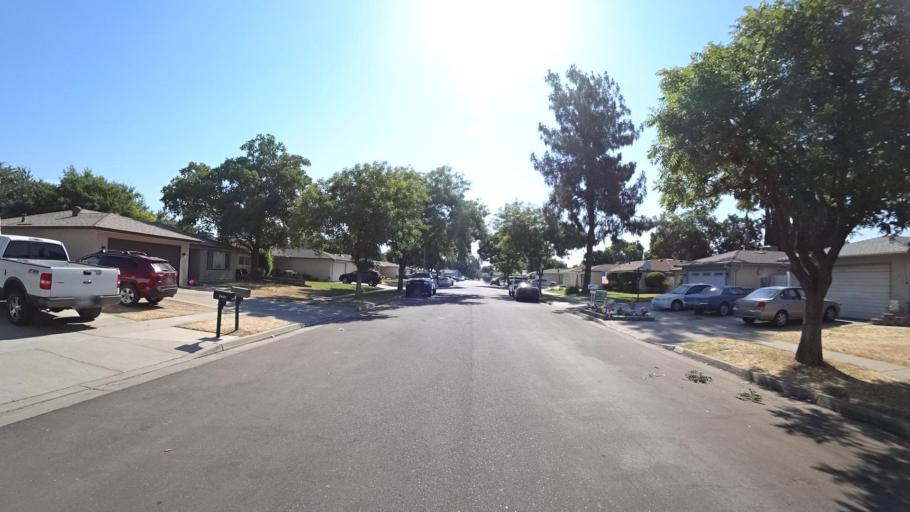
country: US
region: California
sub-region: Fresno County
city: Tarpey Village
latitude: 36.7869
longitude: -119.6896
